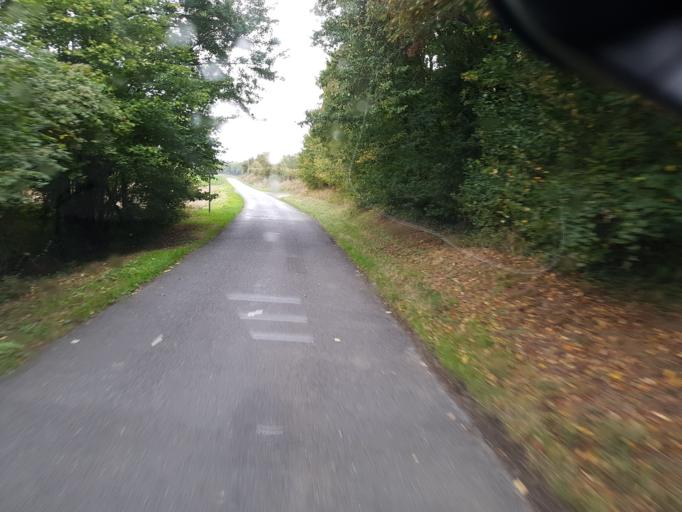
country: FR
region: Picardie
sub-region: Departement de l'Oise
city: Breteuil
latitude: 49.6822
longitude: 2.3315
